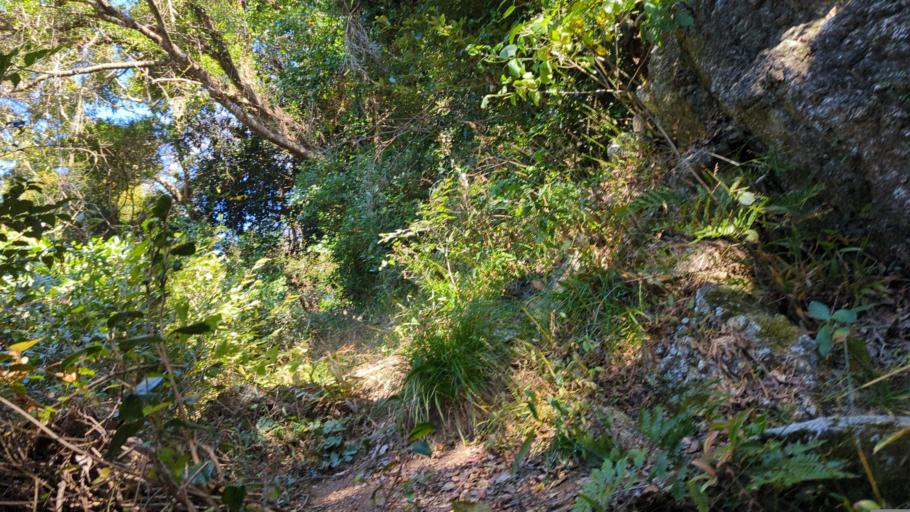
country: JP
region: Aichi
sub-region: Tokai-shi
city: Toyokawa
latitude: 34.7728
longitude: 137.4688
